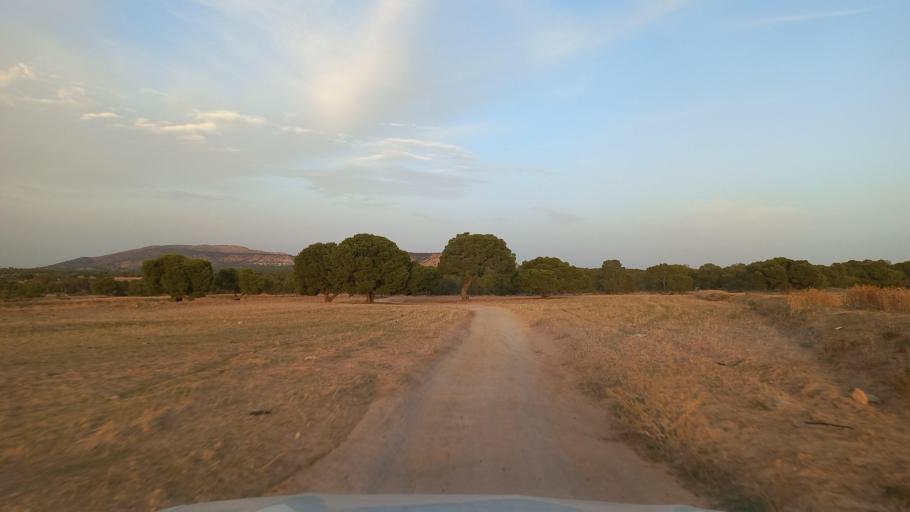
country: TN
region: Al Qasrayn
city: Sbiba
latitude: 35.4246
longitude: 8.9152
